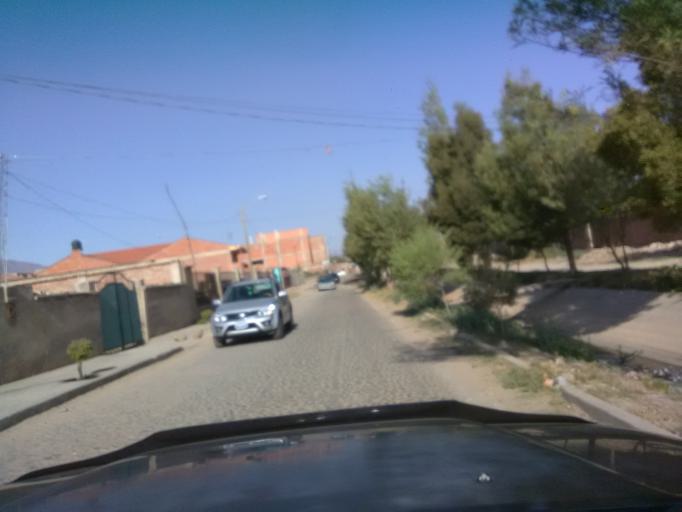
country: BO
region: Cochabamba
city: Cochabamba
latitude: -17.3581
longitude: -66.1924
